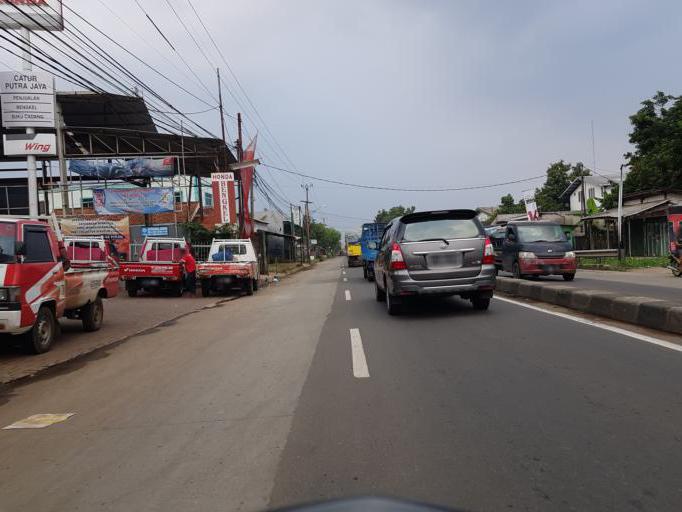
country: ID
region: West Java
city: Ciampea
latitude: -6.5114
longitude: 106.7574
